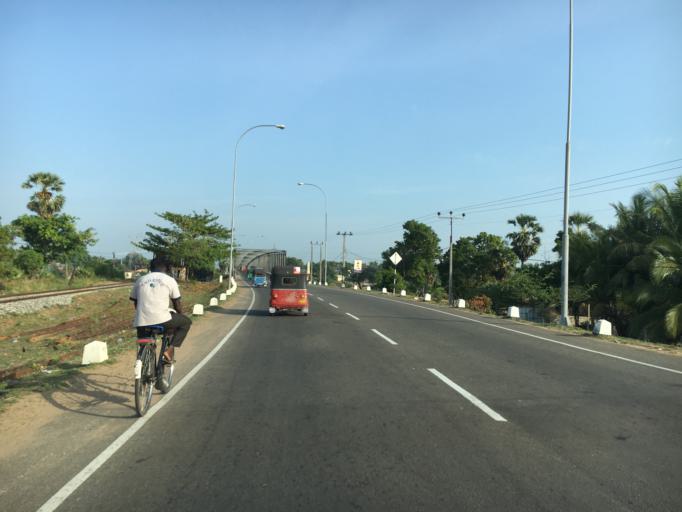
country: LK
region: Eastern Province
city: Eravur Town
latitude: 7.9202
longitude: 81.5165
